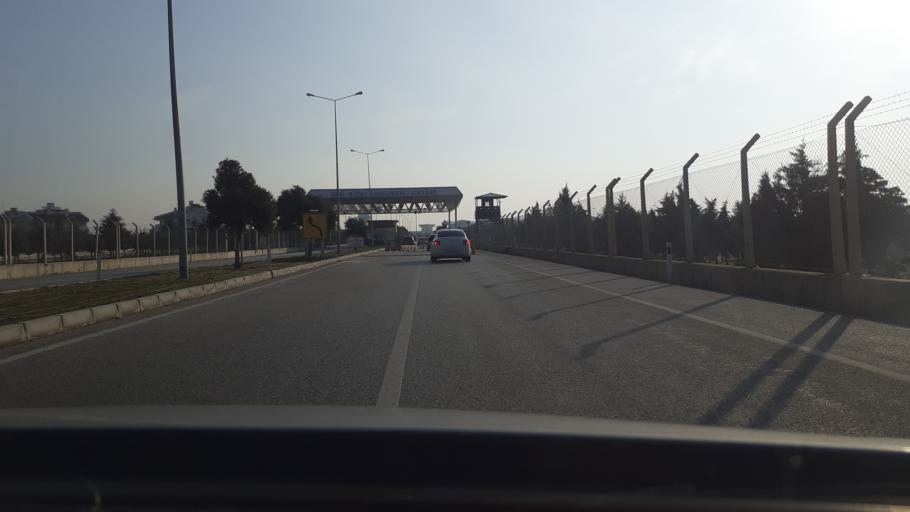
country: TR
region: Hatay
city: Serinyol
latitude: 36.3644
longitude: 36.2747
